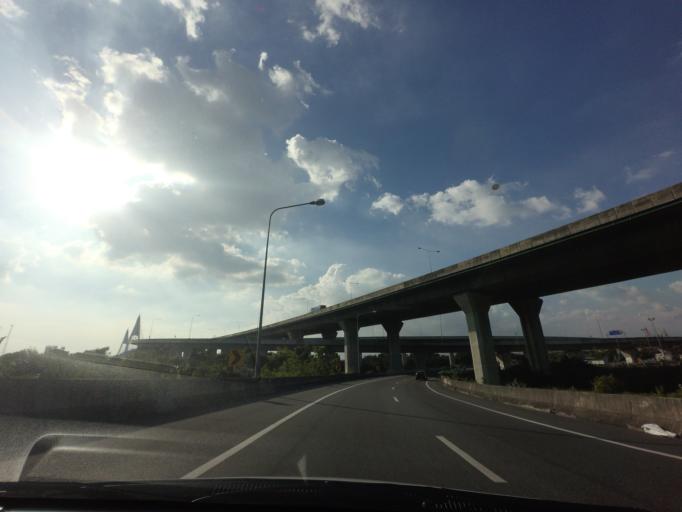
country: TH
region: Samut Prakan
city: Phra Pradaeng
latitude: 13.6381
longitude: 100.5511
